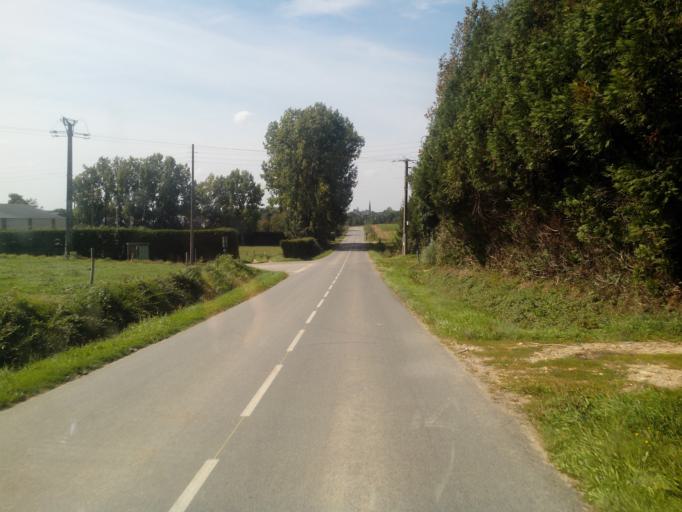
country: FR
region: Brittany
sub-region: Departement d'Ille-et-Vilaine
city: Gael
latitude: 48.1306
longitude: -2.2005
